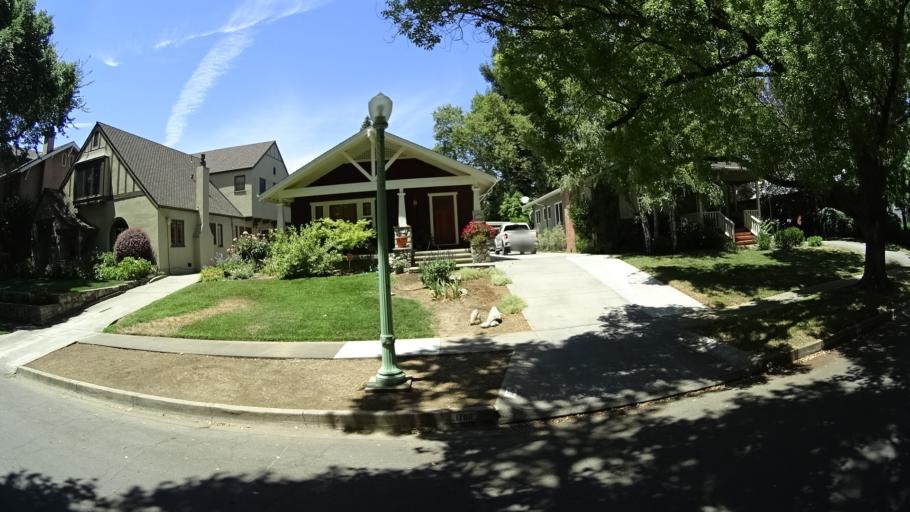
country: US
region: California
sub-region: Sacramento County
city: Sacramento
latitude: 38.5623
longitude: -121.4587
